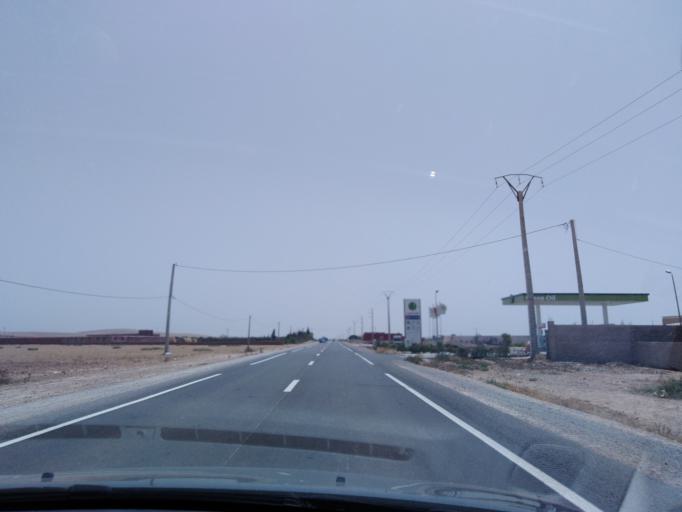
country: MA
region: Doukkala-Abda
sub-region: Safi
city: Youssoufia
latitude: 32.0580
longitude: -8.5669
